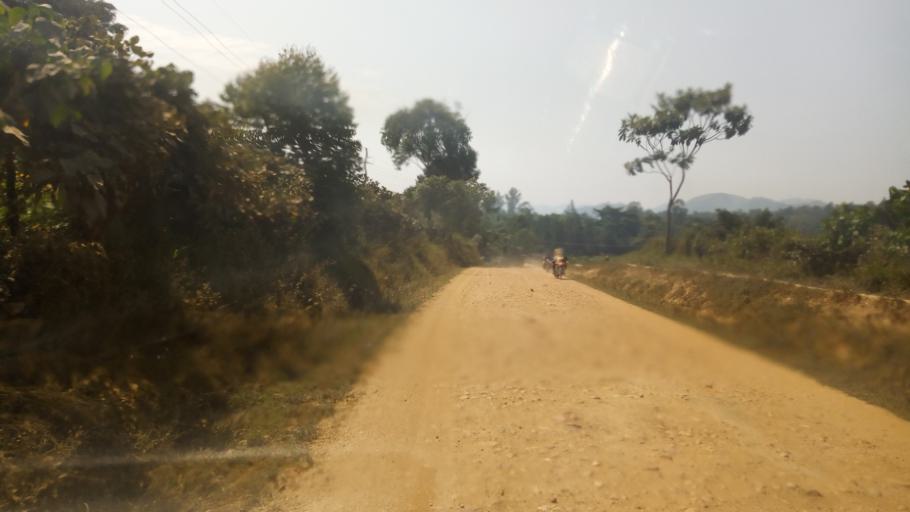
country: UG
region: Western Region
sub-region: Kanungu District
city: Ntungamo
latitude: -0.9127
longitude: 29.6220
